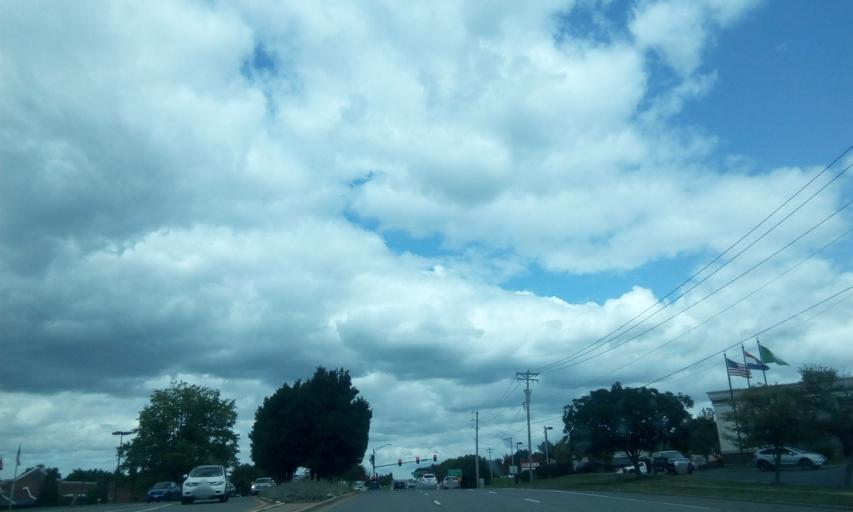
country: US
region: Missouri
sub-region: Saint Louis County
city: Chesterfield
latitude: 38.6426
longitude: -90.5670
